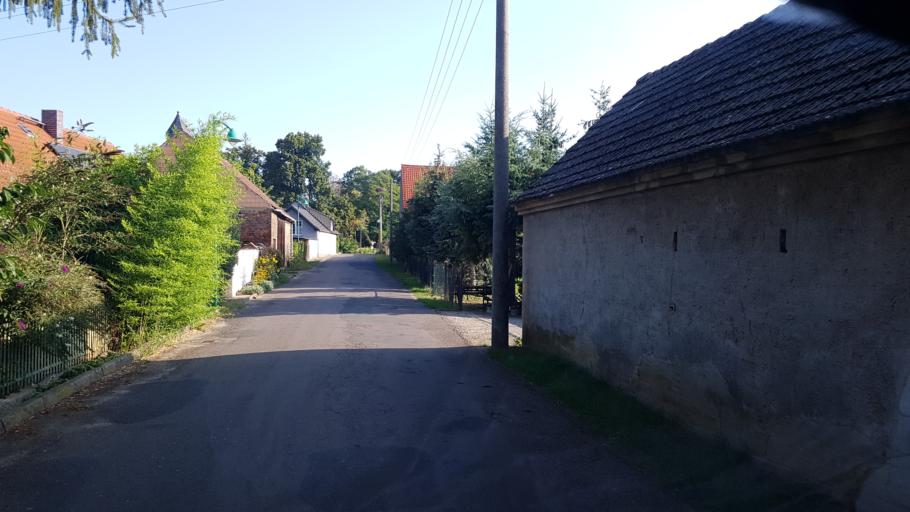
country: DE
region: Brandenburg
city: Luckau
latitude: 51.8020
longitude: 13.6493
